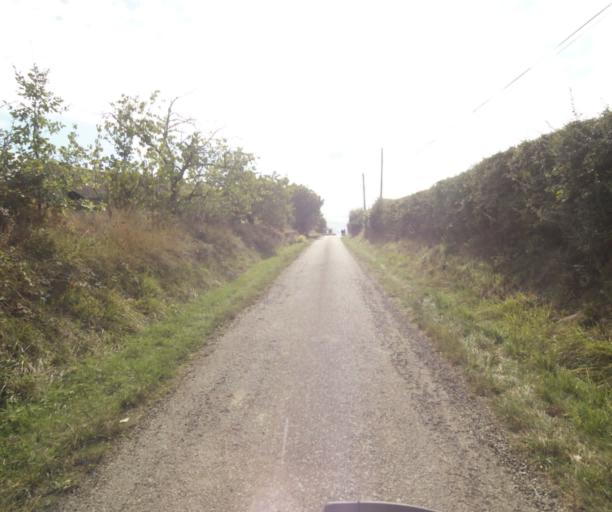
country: FR
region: Midi-Pyrenees
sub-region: Departement du Tarn-et-Garonne
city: Verdun-sur-Garonne
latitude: 43.8628
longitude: 1.1803
